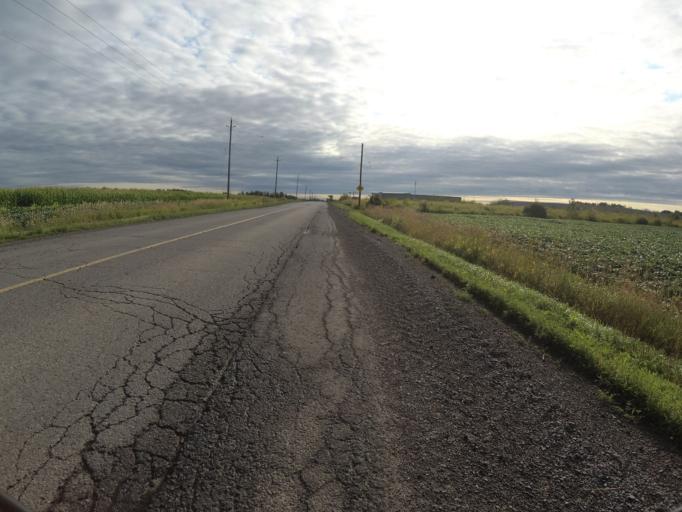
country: CA
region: Ontario
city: Clarence-Rockland
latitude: 45.3261
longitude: -75.3748
